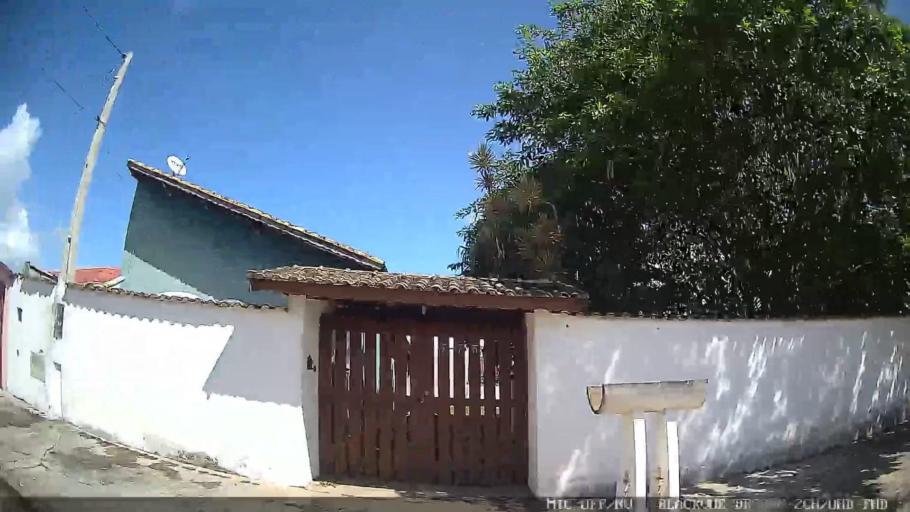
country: BR
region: Sao Paulo
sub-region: Itanhaem
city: Itanhaem
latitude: -24.2293
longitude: -46.8773
